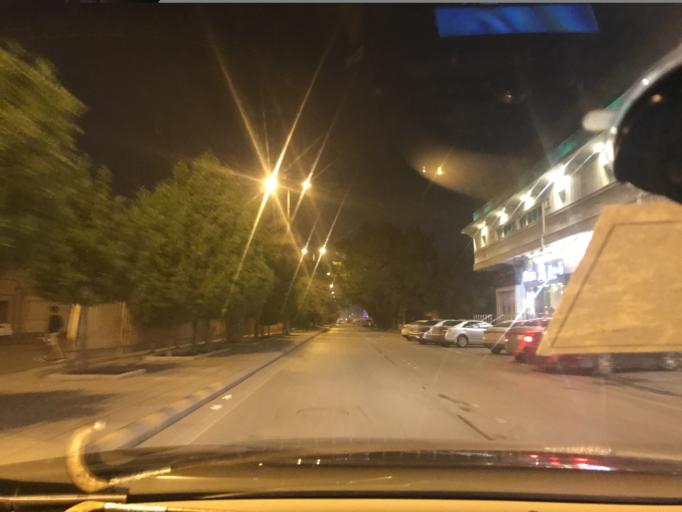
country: SA
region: Ar Riyad
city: Riyadh
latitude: 24.7090
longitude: 46.7740
